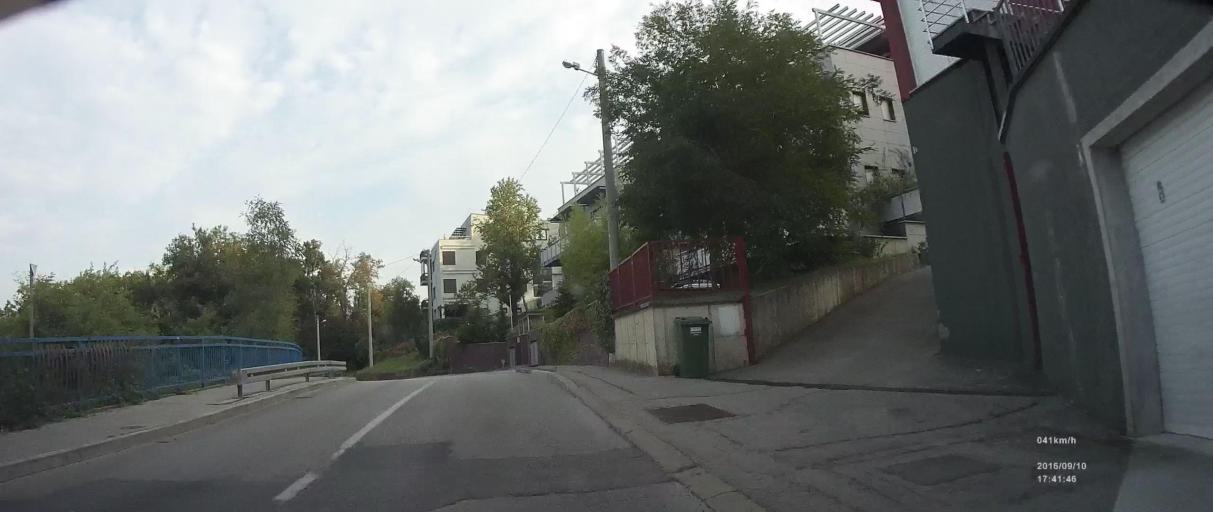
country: HR
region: Grad Zagreb
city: Zagreb
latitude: 45.8325
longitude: 15.9389
